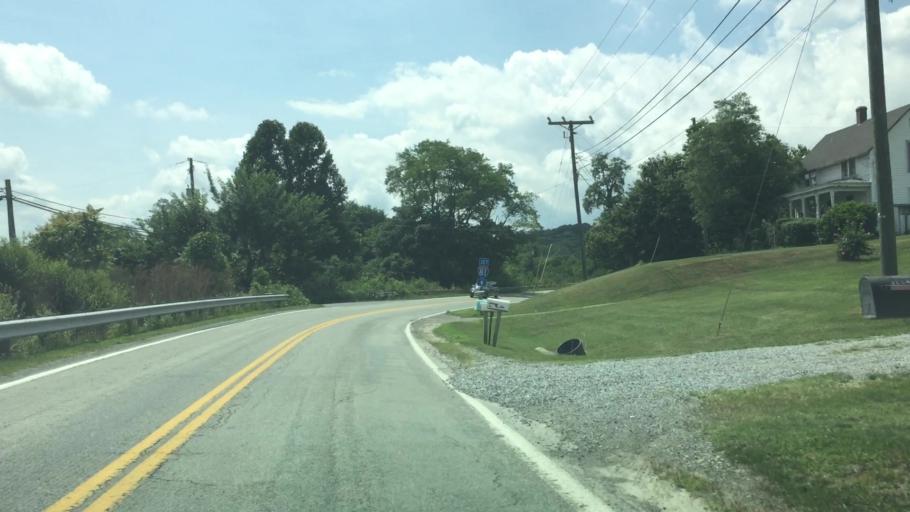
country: US
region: Virginia
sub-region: Pulaski County
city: Pulaski
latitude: 37.0057
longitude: -80.7494
